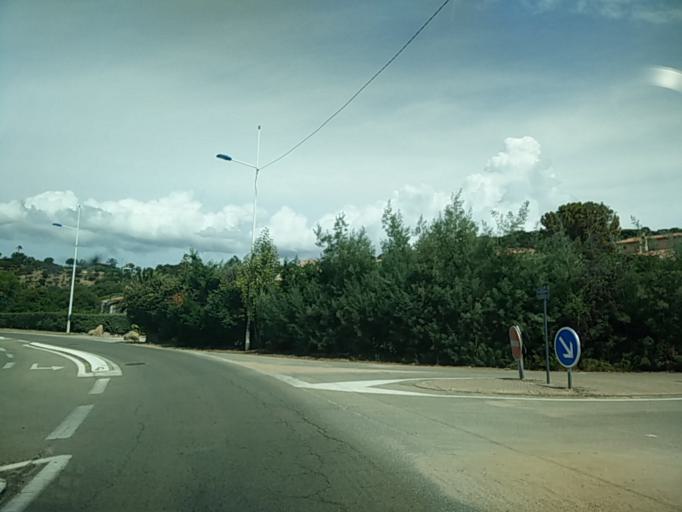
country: FR
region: Corsica
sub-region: Departement de la Corse-du-Sud
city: Pietrosella
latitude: 41.8714
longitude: 8.7876
